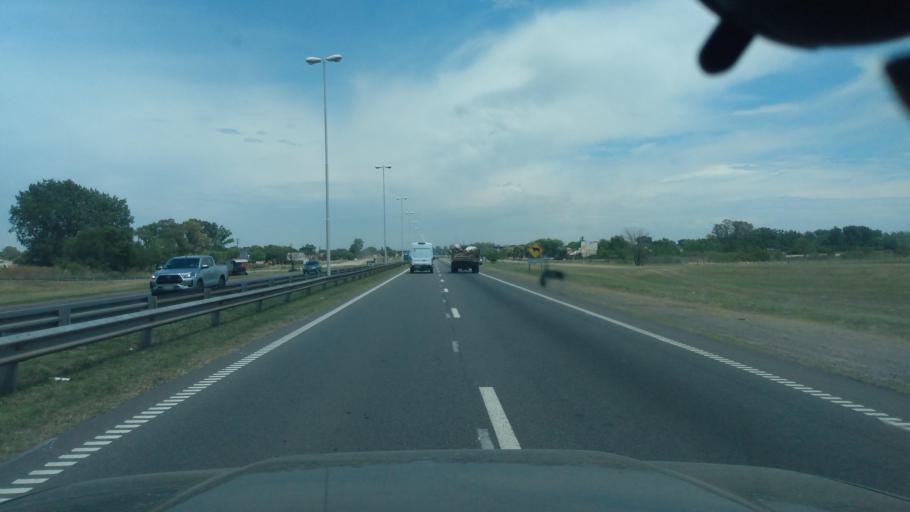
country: AR
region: Buenos Aires
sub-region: Partido de Lujan
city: Lujan
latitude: -34.5653
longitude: -59.0754
